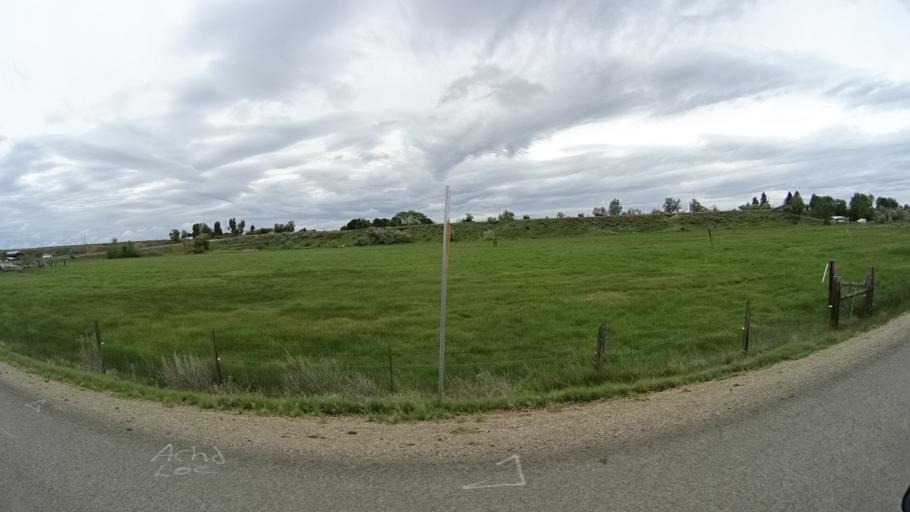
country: US
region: Idaho
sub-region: Ada County
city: Star
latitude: 43.6708
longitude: -116.4954
